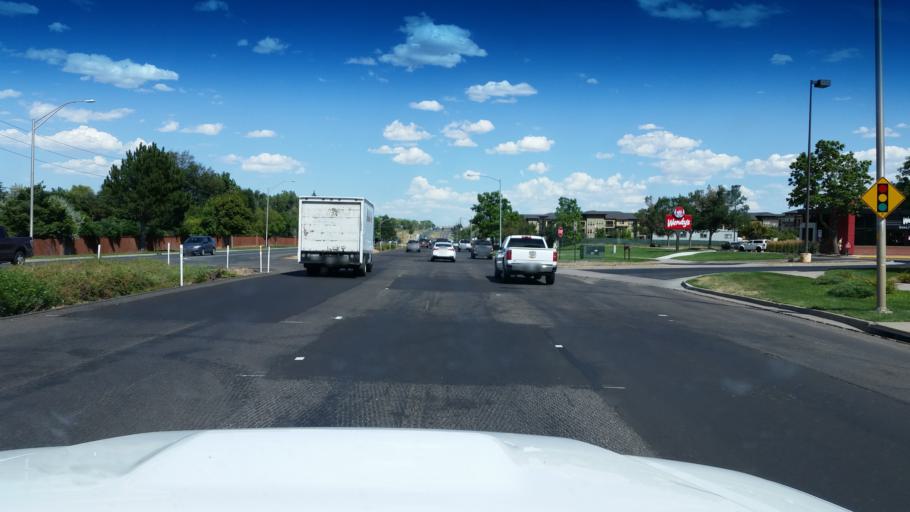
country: US
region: Colorado
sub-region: Adams County
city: Thornton
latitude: 39.8850
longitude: -104.9690
